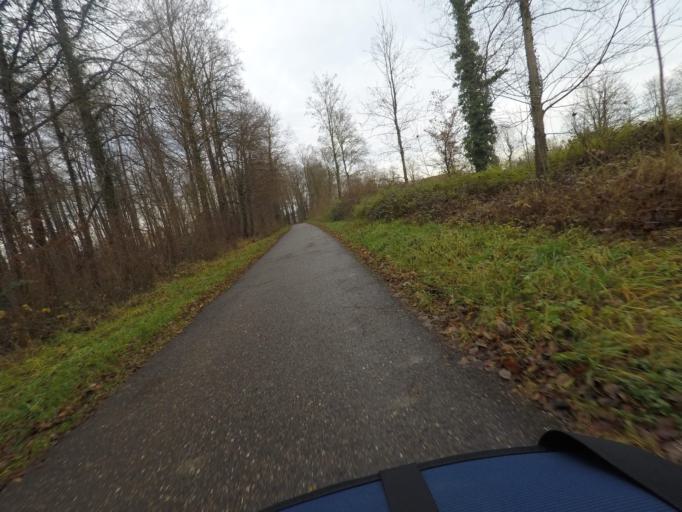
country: DE
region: Baden-Wuerttemberg
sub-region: Karlsruhe Region
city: Rheinau
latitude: 48.8567
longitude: 8.1628
